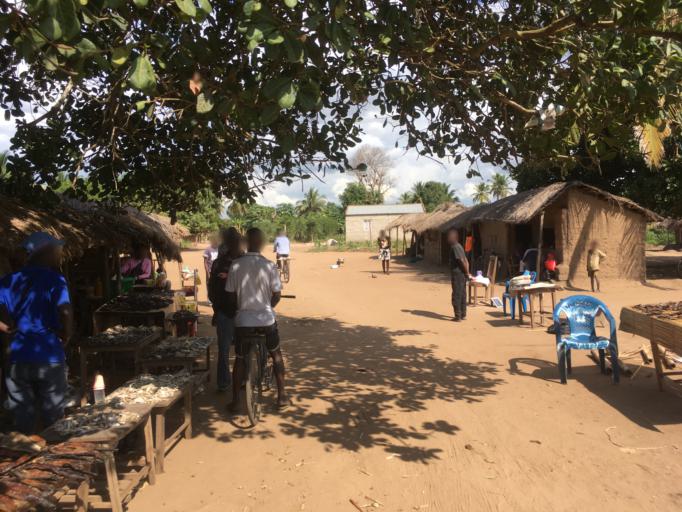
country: MZ
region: Zambezia
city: Quelimane
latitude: -17.6499
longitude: 36.6849
